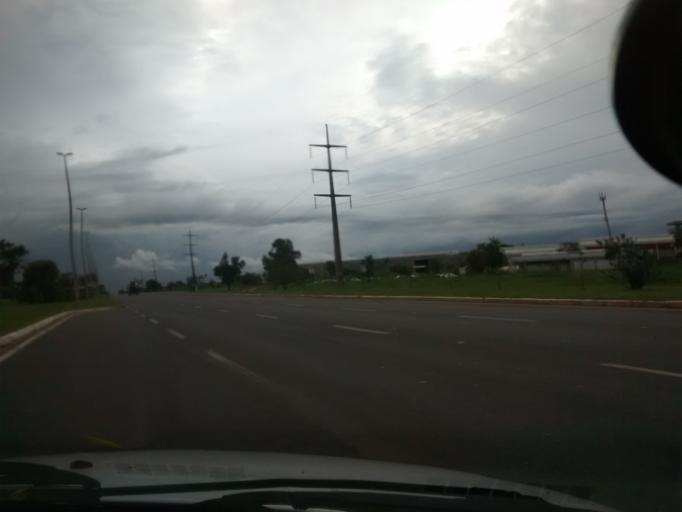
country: BR
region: Federal District
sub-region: Brasilia
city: Brasilia
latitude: -15.7654
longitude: -47.8630
